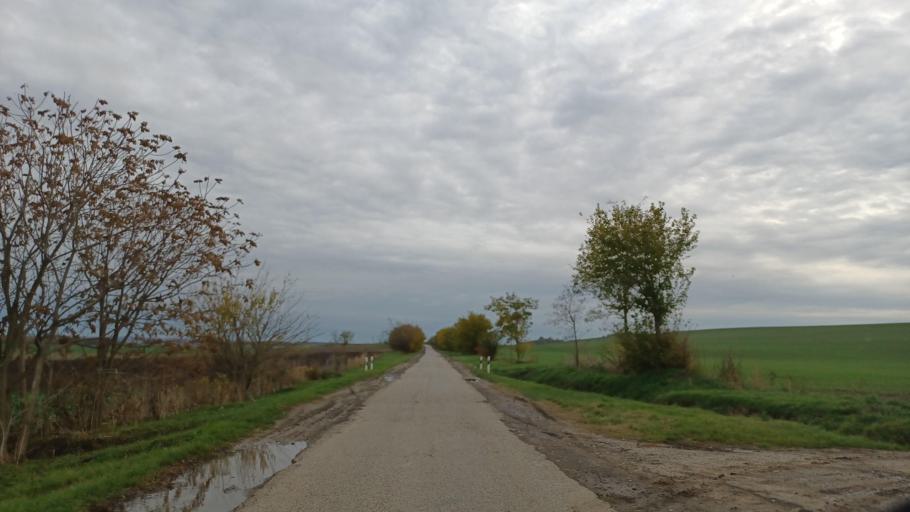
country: HU
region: Tolna
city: Simontornya
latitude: 46.7025
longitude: 18.5856
